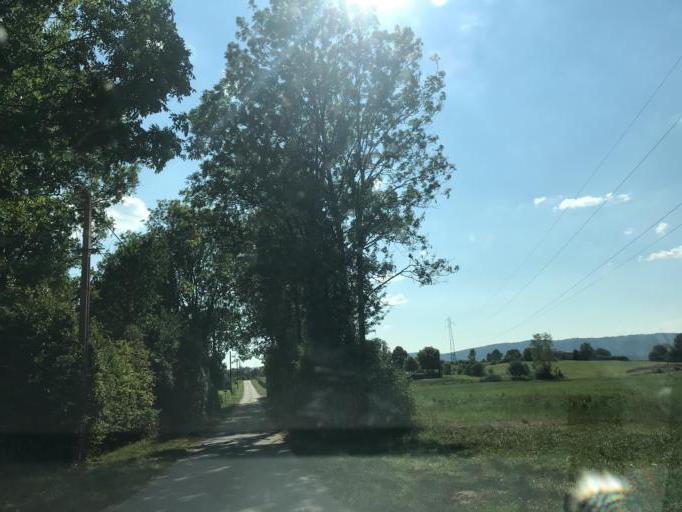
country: FR
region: Franche-Comte
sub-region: Departement du Jura
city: Clairvaux-les-Lacs
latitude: 46.5809
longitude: 5.7280
